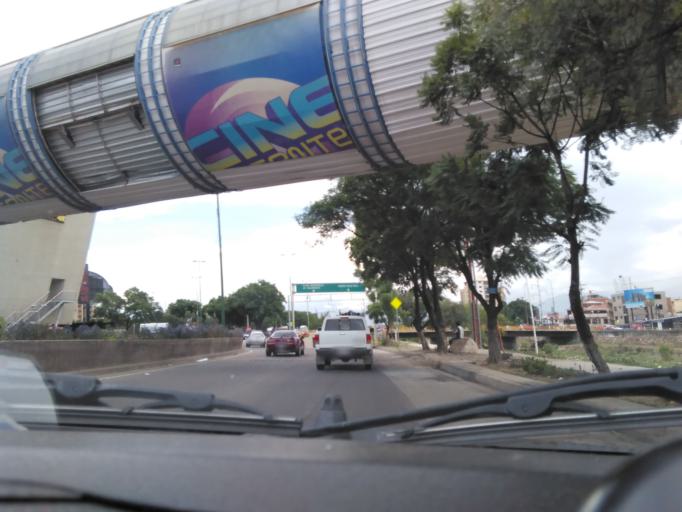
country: BO
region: Cochabamba
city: Cochabamba
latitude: -17.3794
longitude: -66.1508
